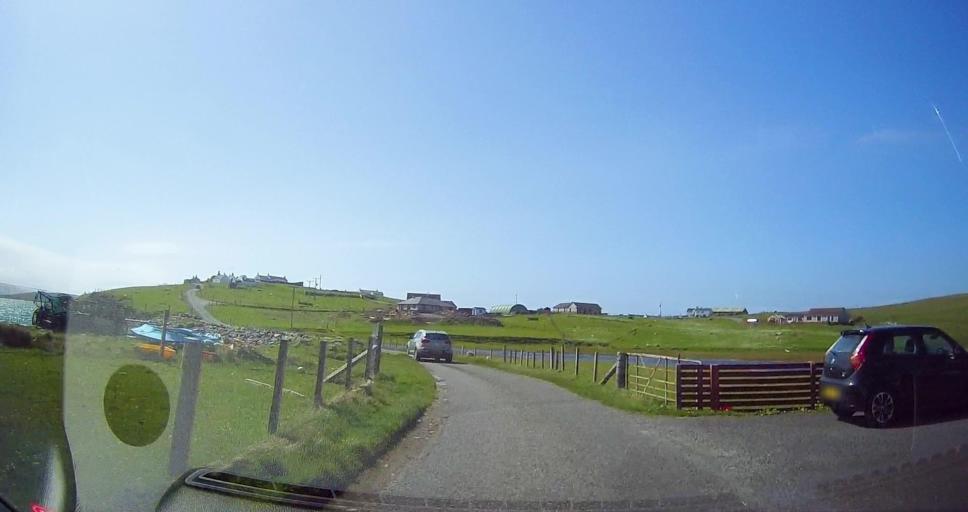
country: GB
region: Scotland
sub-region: Shetland Islands
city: Sandwick
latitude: 60.0649
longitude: -1.3392
